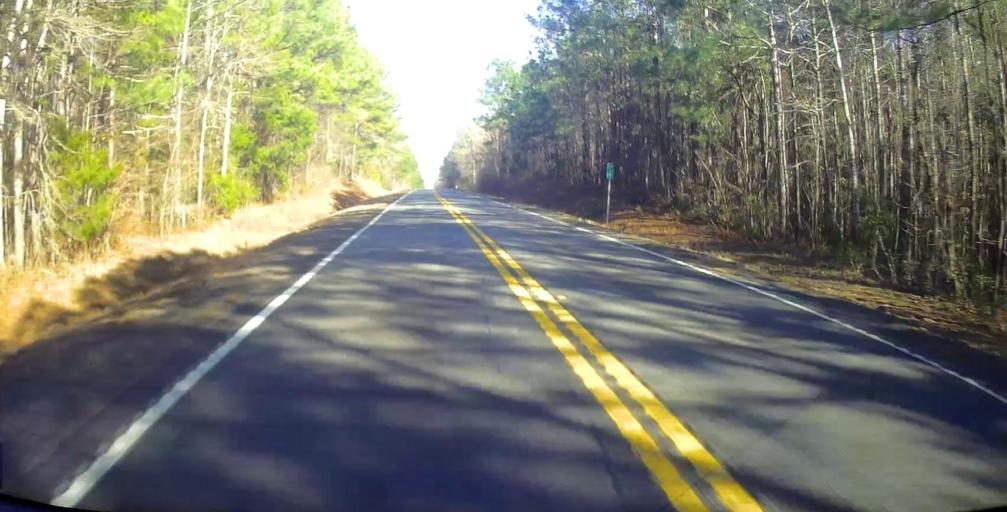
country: US
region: Georgia
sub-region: Talbot County
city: Talbotton
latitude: 32.6725
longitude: -84.5106
